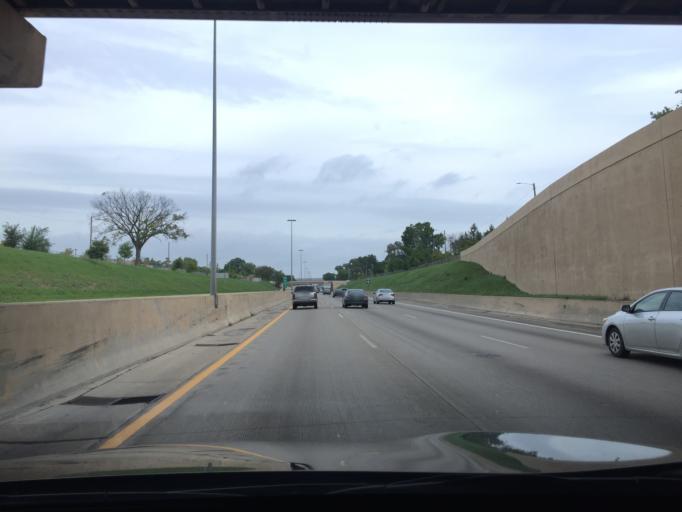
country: US
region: Michigan
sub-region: Oakland County
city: Oak Park
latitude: 42.4191
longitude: -83.2189
